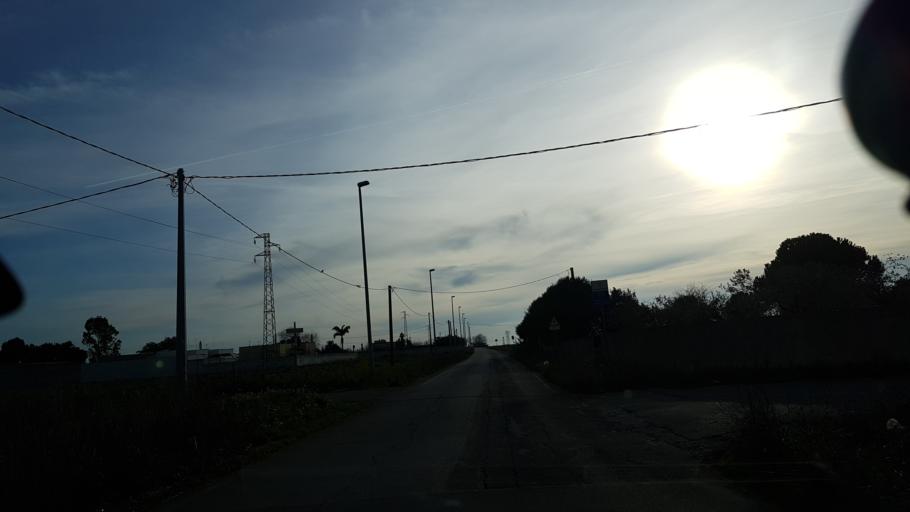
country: IT
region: Apulia
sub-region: Provincia di Brindisi
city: Brindisi
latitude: 40.6144
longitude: 17.9161
